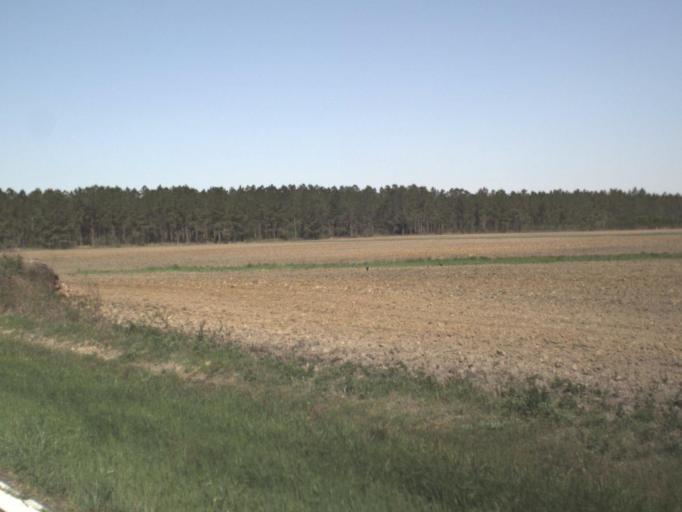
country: US
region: Florida
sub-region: Jackson County
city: Graceville
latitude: 30.9540
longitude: -85.4633
